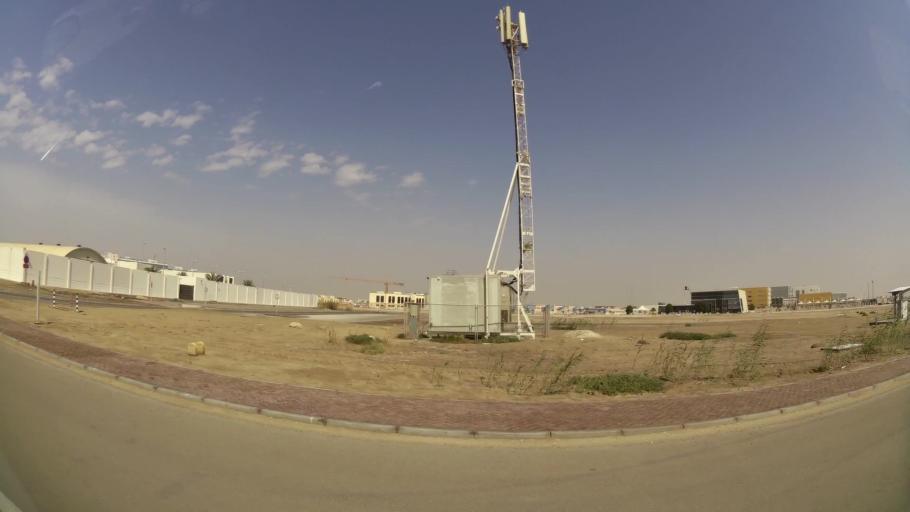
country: AE
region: Abu Dhabi
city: Abu Dhabi
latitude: 24.3137
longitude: 54.5548
